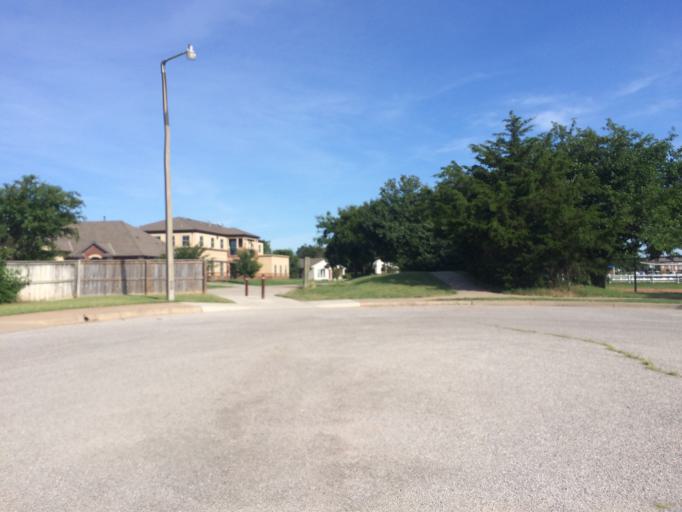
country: US
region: Oklahoma
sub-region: Cleveland County
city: Norman
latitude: 35.2296
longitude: -97.4777
